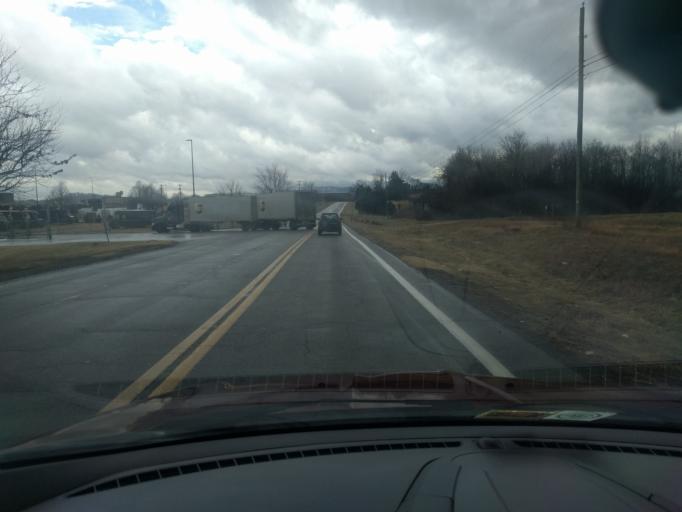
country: US
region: Virginia
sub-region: Roanoke County
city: Hollins
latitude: 37.3196
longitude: -79.9812
